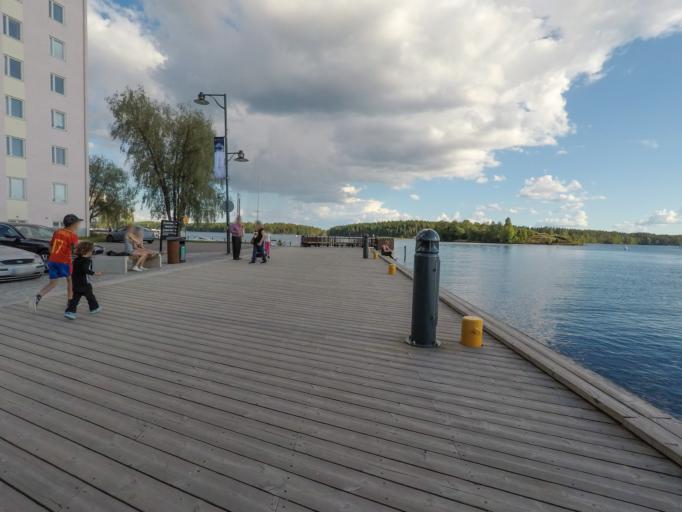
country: FI
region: Southern Savonia
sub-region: Savonlinna
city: Savonlinna
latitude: 61.8656
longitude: 28.8866
